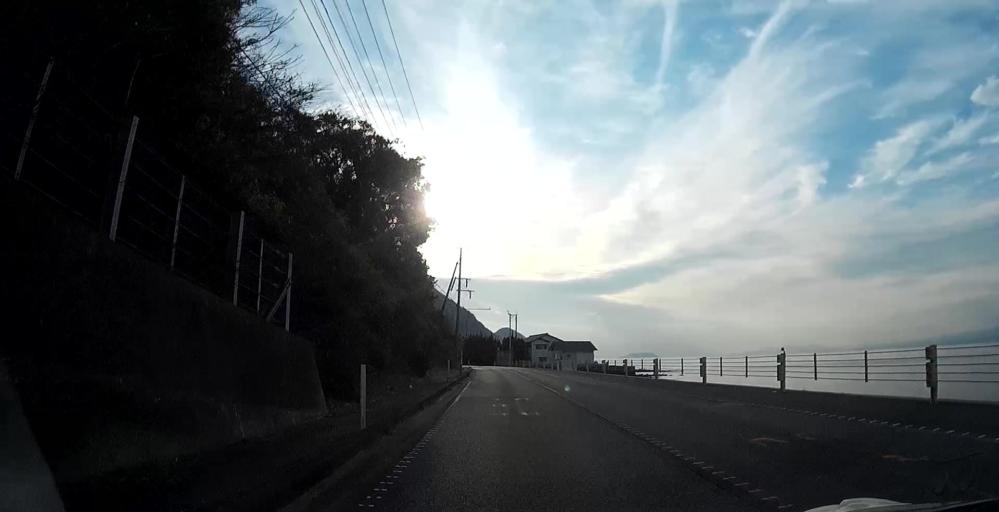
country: JP
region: Nagasaki
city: Shimabara
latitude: 32.6430
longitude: 130.4806
